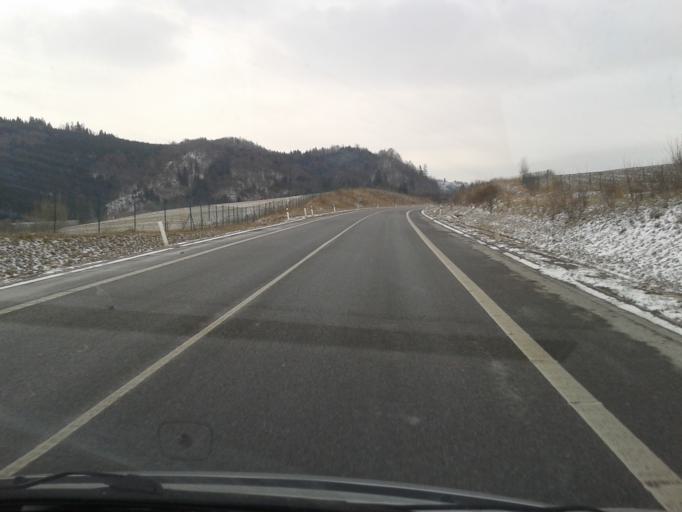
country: SK
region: Zilinsky
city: Tvrdosin
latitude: 49.3484
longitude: 19.5830
